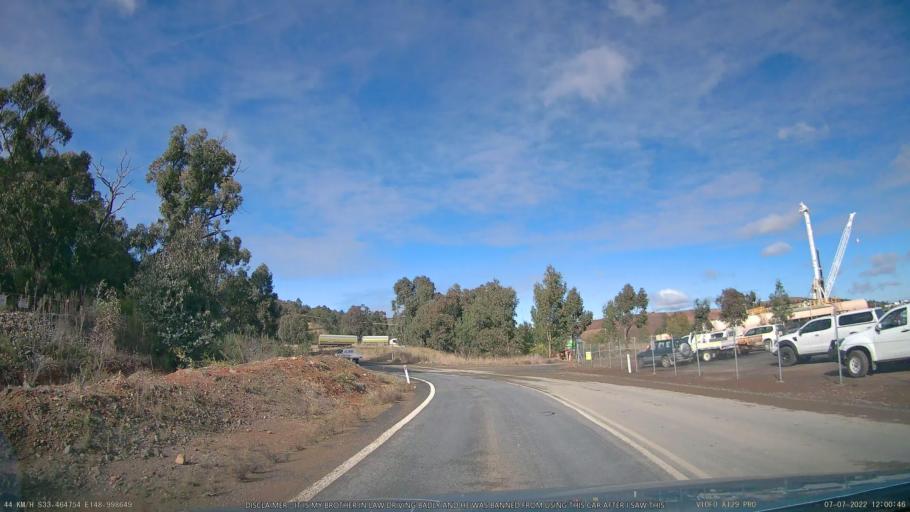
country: AU
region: New South Wales
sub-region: Blayney
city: Millthorpe
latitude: -33.4650
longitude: 148.9987
